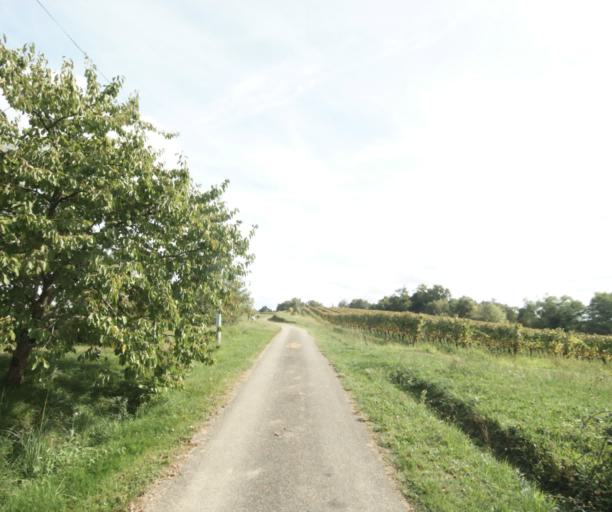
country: FR
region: Midi-Pyrenees
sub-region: Departement du Gers
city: Eauze
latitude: 43.8361
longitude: 0.1408
